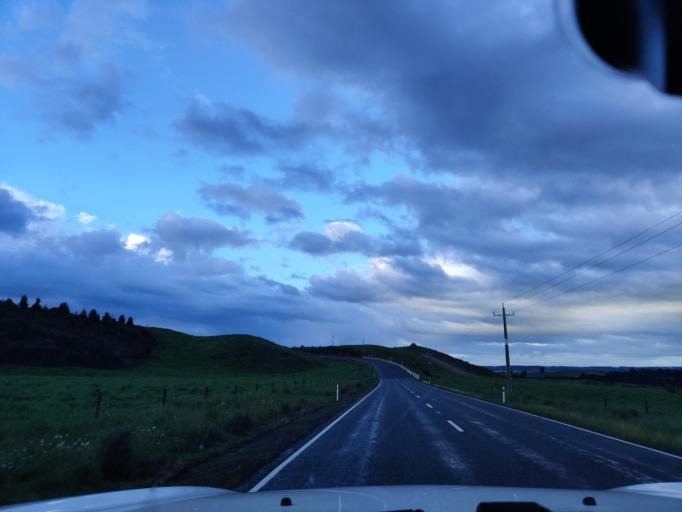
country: NZ
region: Waikato
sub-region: South Waikato District
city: Tokoroa
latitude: -38.3840
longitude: 175.7834
